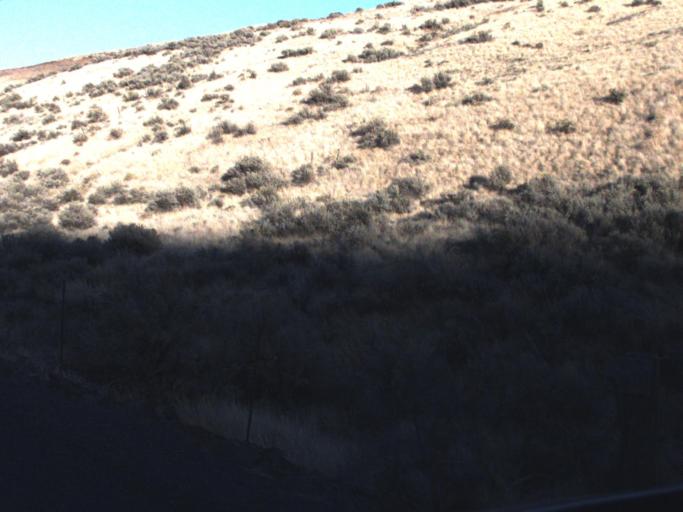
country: US
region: Washington
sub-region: Franklin County
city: Connell
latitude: 46.6773
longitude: -118.5409
